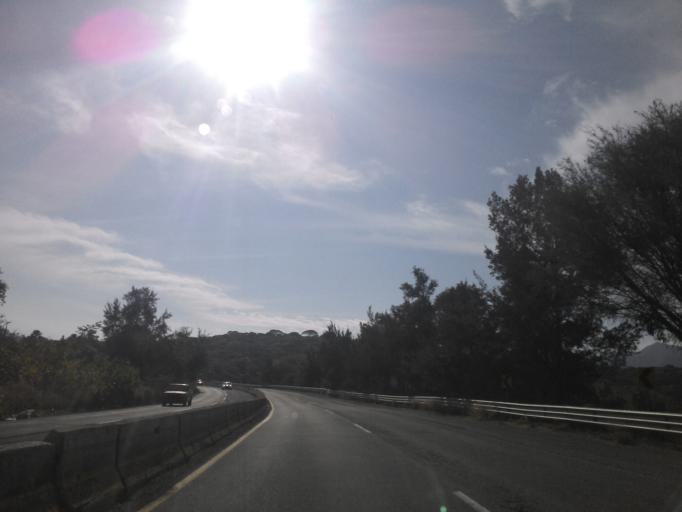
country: MX
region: Jalisco
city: Ixtlahuacan de los Membrillos
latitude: 20.3259
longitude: -103.1954
